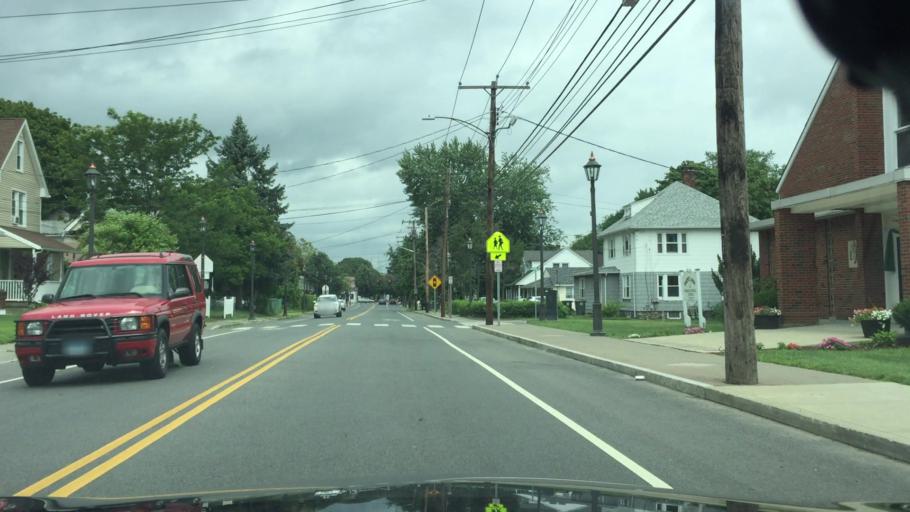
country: US
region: Connecticut
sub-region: Fairfield County
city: Stratford
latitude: 41.2002
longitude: -73.1006
